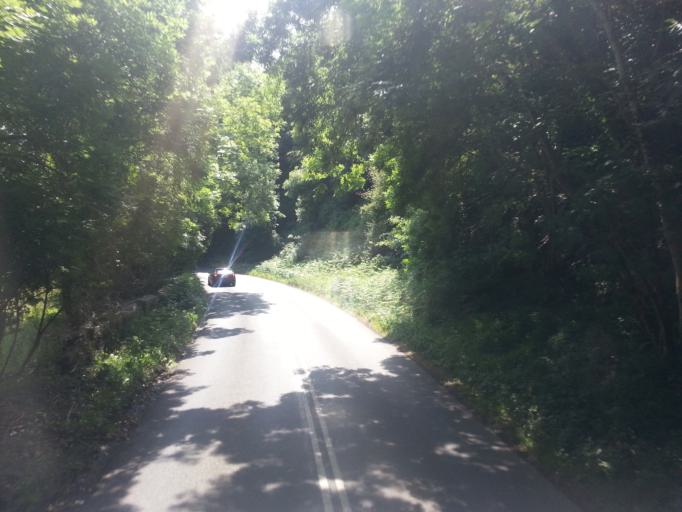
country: IE
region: Leinster
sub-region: Wicklow
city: Enniskerry
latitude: 53.2166
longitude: -6.1791
